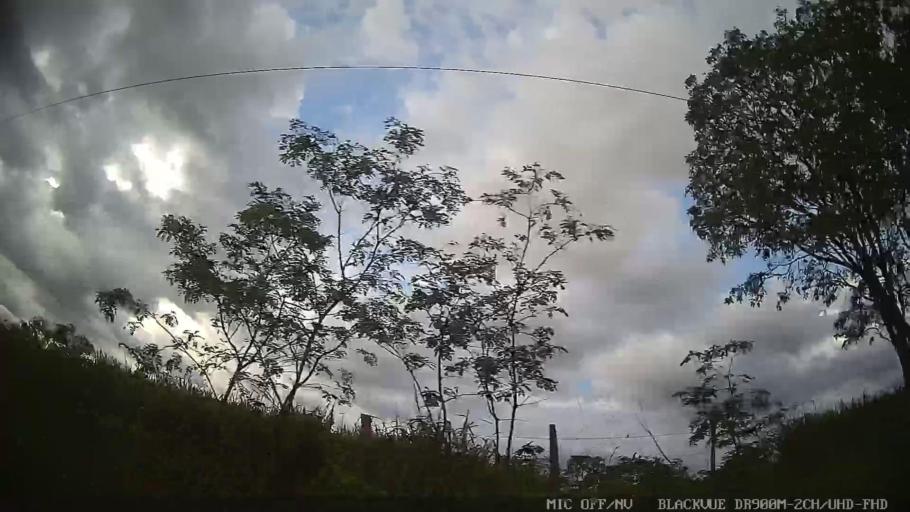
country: BR
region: Sao Paulo
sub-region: Jaguariuna
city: Jaguariuna
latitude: -22.7239
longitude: -47.0015
